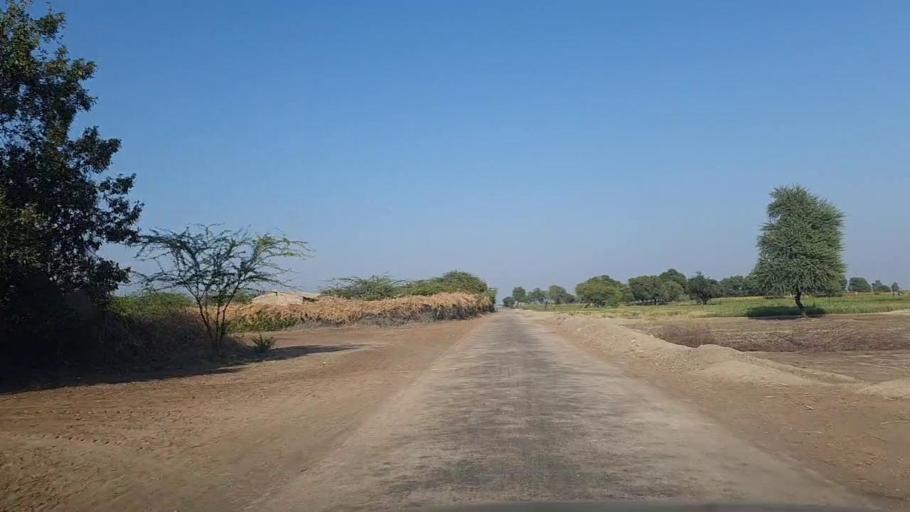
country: PK
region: Sindh
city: Digri
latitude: 25.0253
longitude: 69.2524
